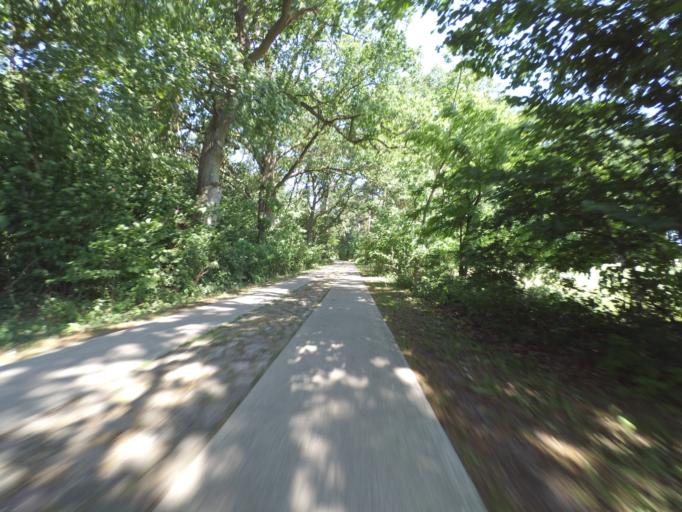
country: DE
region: Brandenburg
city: Heiligengrabe
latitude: 53.2381
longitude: 12.3149
